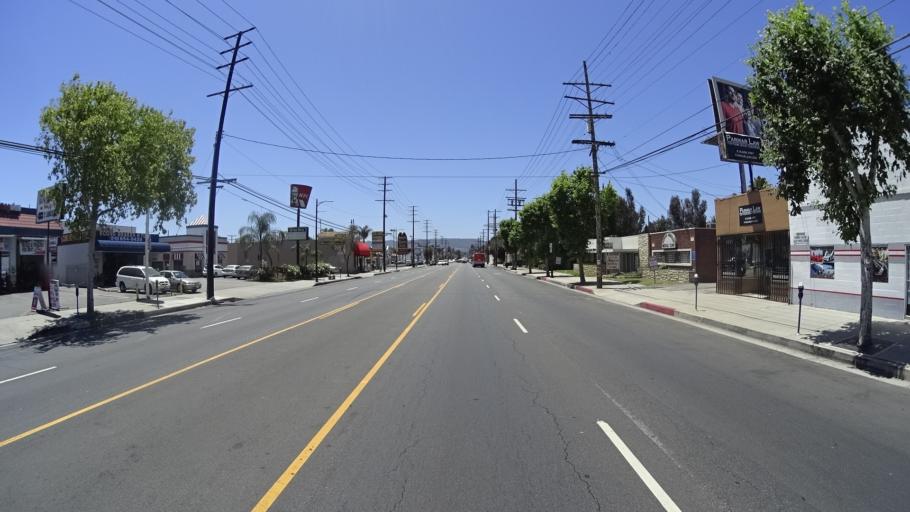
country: US
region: California
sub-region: Los Angeles County
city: Northridge
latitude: 34.1967
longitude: -118.5361
